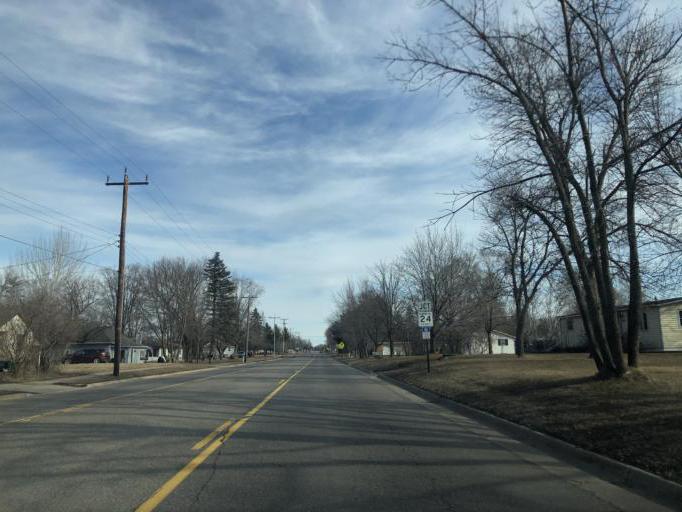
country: US
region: Minnesota
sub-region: Sherburne County
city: Becker
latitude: 45.3919
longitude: -93.8704
